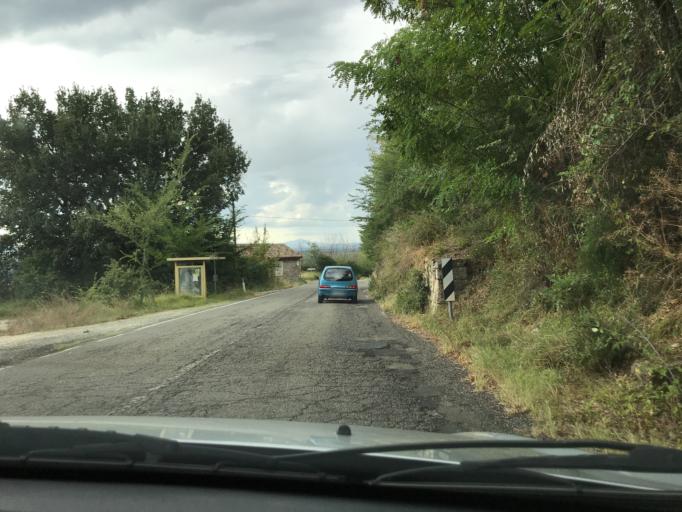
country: IT
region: Umbria
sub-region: Provincia di Terni
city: Montecchio
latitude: 42.6452
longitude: 12.2813
